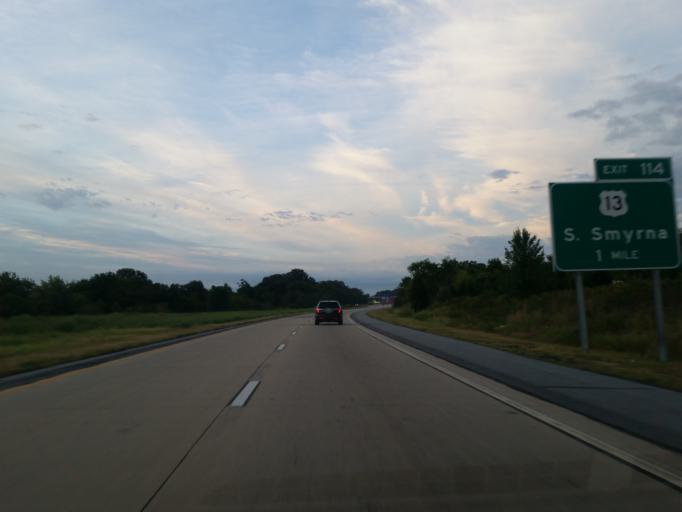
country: US
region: Delaware
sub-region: Kent County
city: Smyrna
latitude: 39.3022
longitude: -75.5935
